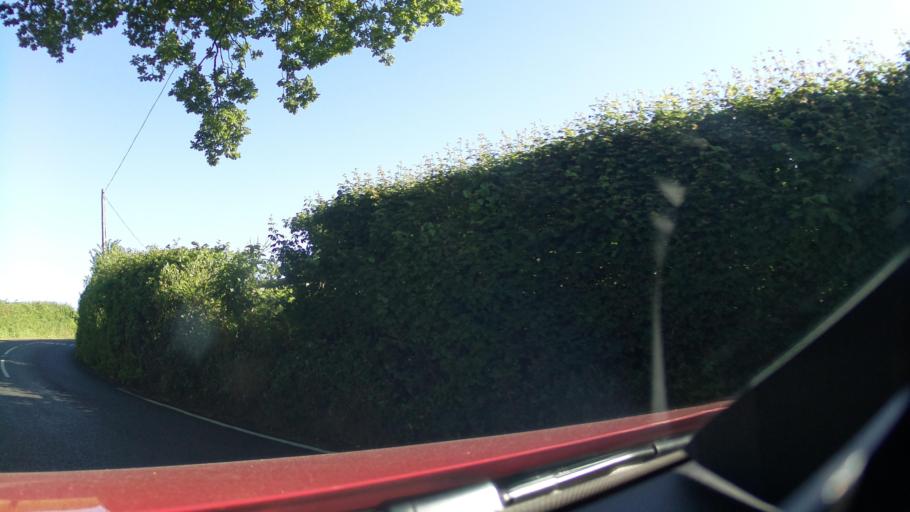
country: GB
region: England
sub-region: Somerset
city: Crewkerne
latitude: 50.8316
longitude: -2.8564
